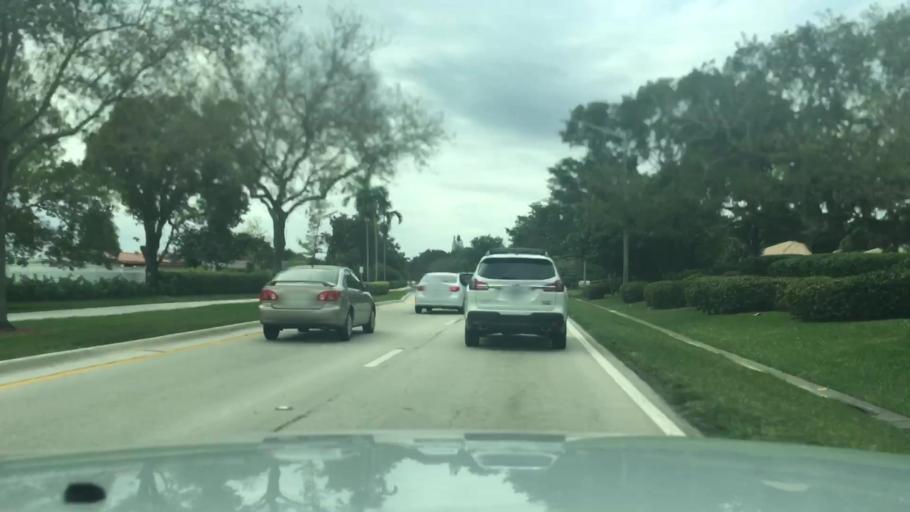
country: US
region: Florida
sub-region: Broward County
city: Margate
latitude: 26.2529
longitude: -80.2393
